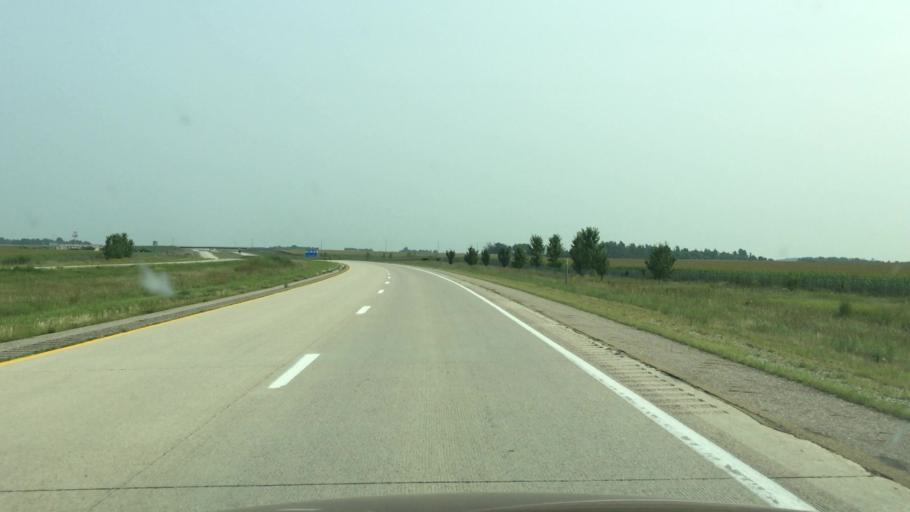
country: US
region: Iowa
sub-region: Osceola County
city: Sibley
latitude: 43.3930
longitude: -95.7180
